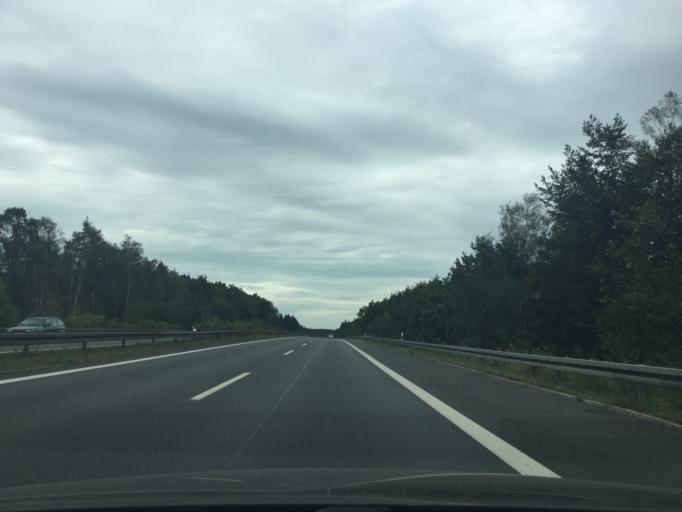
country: DE
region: Saxony
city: Hirschfeld
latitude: 50.6259
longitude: 12.4189
